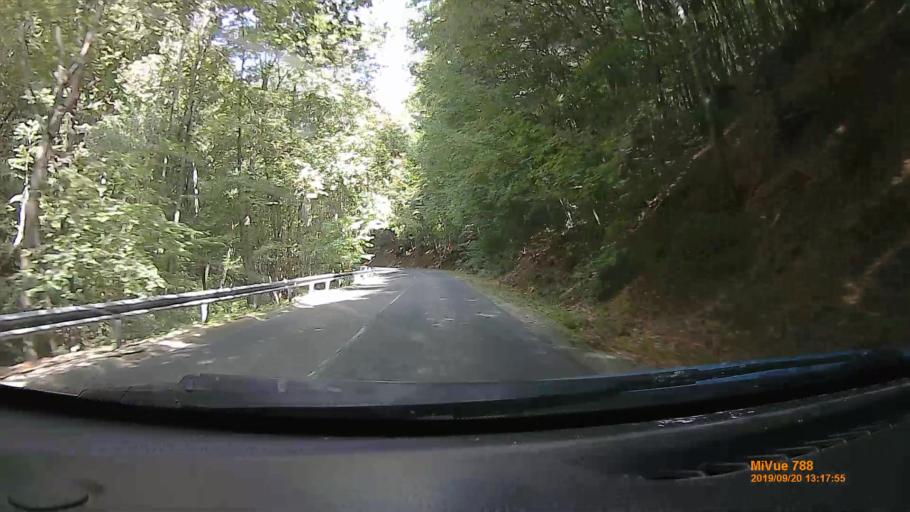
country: HU
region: Heves
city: Felsotarkany
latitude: 47.9966
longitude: 20.4611
